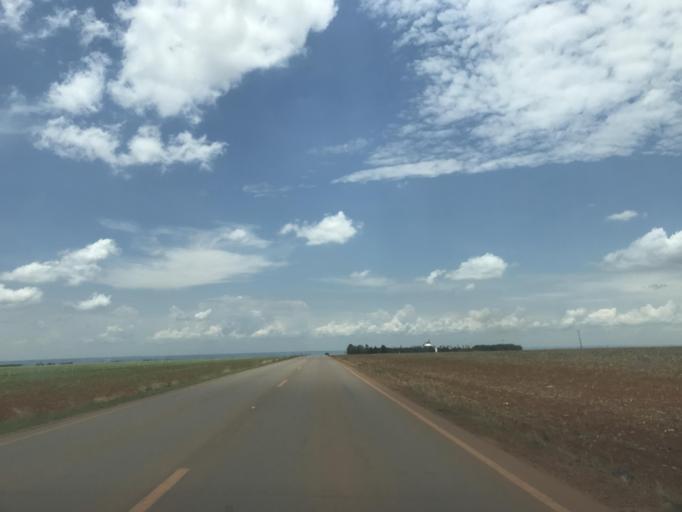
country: BR
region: Goias
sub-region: Vianopolis
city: Vianopolis
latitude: -16.5378
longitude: -48.2545
